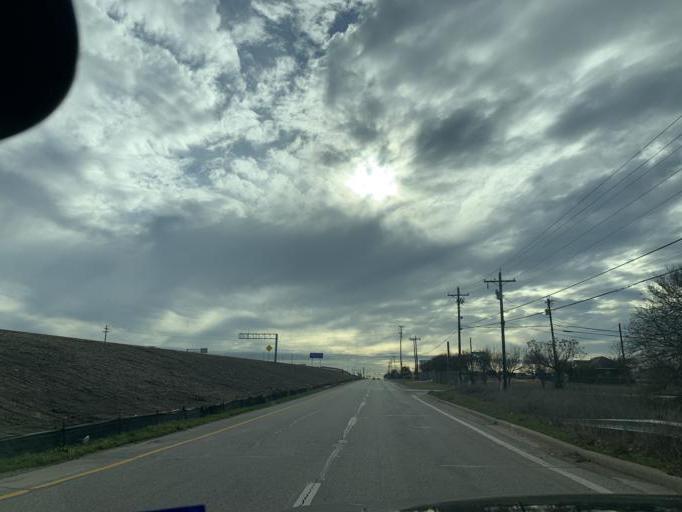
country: US
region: Texas
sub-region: Dallas County
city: Duncanville
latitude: 32.6220
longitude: -96.9124
